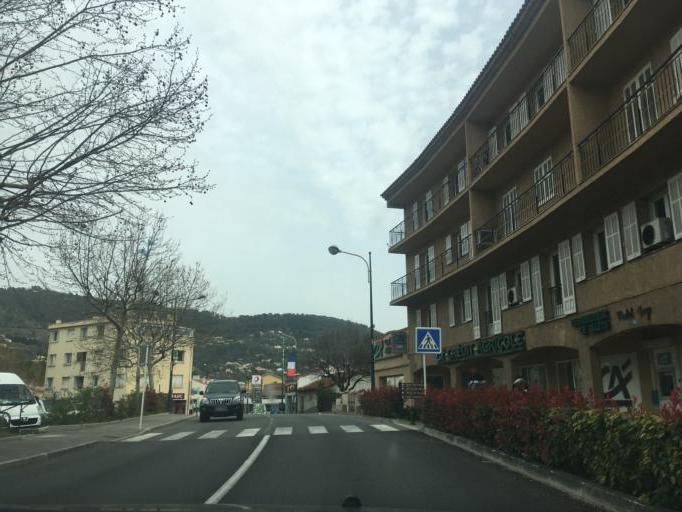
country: FR
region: Provence-Alpes-Cote d'Azur
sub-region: Departement des Alpes-Maritimes
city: Peymeinade
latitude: 43.6394
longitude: 6.8766
